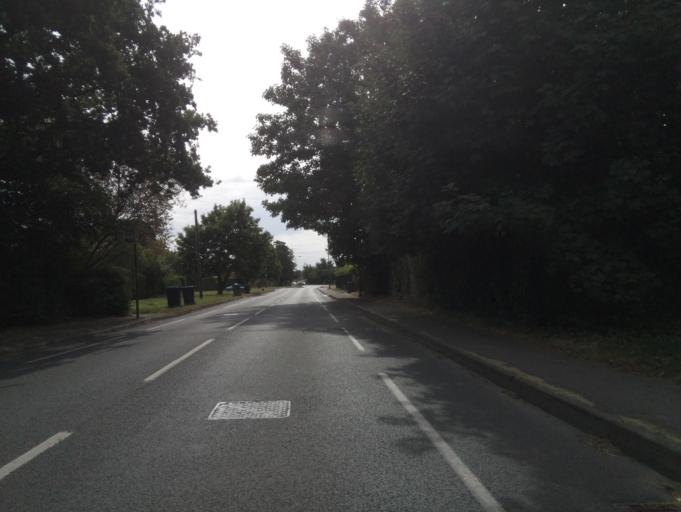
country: GB
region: England
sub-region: West Sussex
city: Copthorne
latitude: 51.1738
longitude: -0.1199
